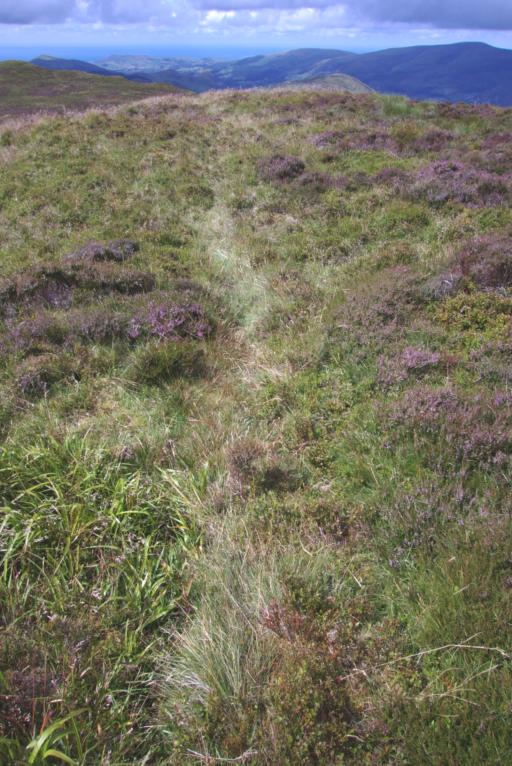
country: GB
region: Wales
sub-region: Gwynedd
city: Corris
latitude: 52.6564
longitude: -3.9065
